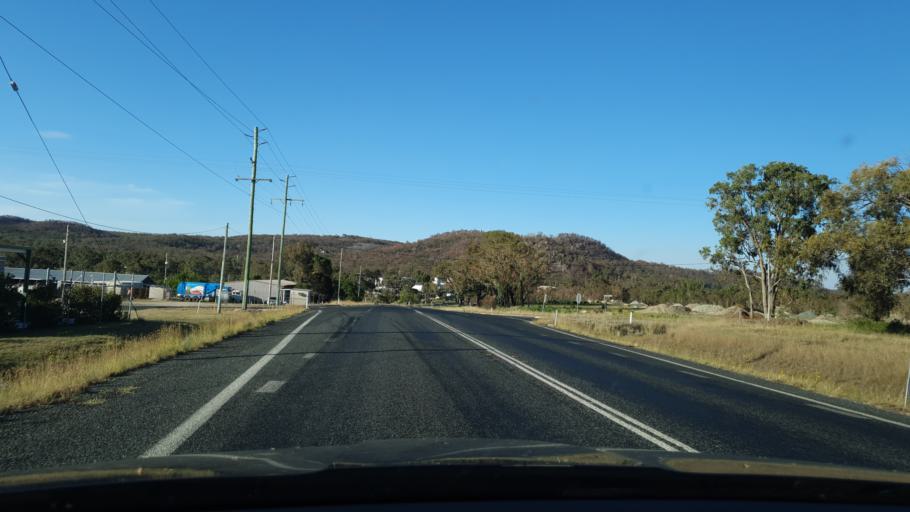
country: AU
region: Queensland
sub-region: Southern Downs
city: Stanthorpe
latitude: -28.6571
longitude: 151.9171
